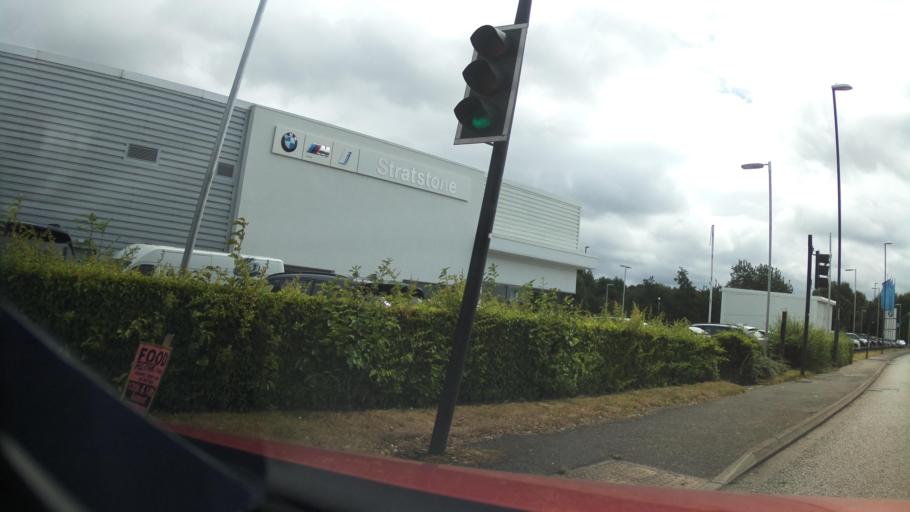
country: GB
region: England
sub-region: Derby
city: Derby
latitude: 52.9407
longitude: -1.4629
